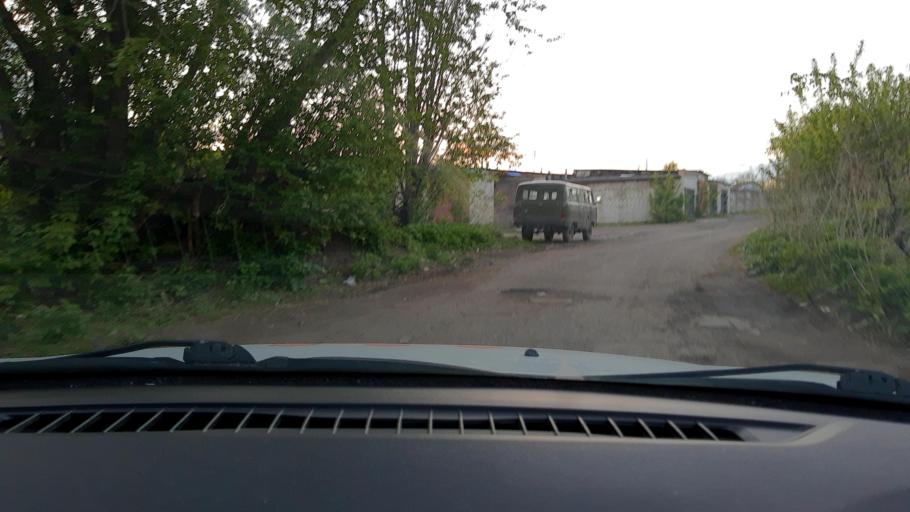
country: RU
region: Nizjnij Novgorod
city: Nizhniy Novgorod
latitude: 56.3058
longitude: 44.0524
